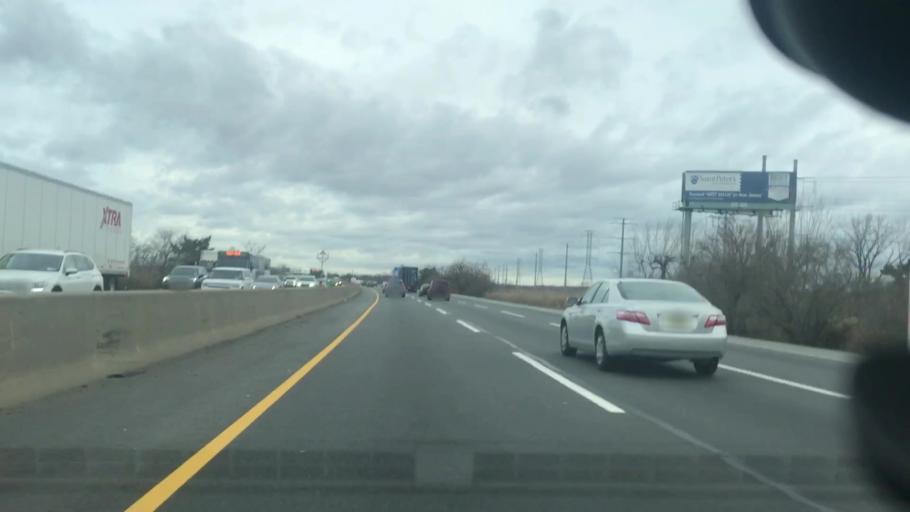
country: US
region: New Jersey
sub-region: Hudson County
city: North Bergen
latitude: 40.8095
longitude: -74.0303
